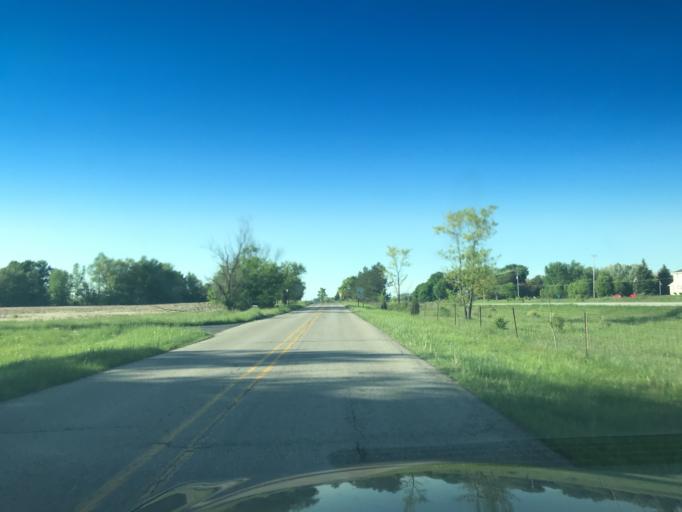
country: US
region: Michigan
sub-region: Ingham County
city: Mason
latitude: 42.5284
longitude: -84.4440
